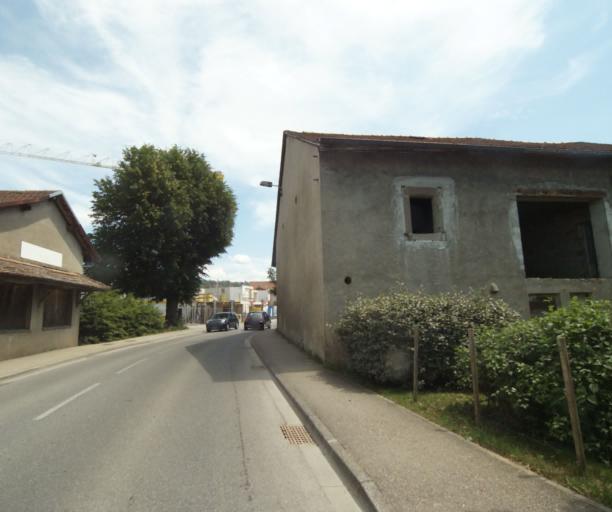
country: FR
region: Rhone-Alpes
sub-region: Departement de la Haute-Savoie
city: Douvaine
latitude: 46.3067
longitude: 6.2972
